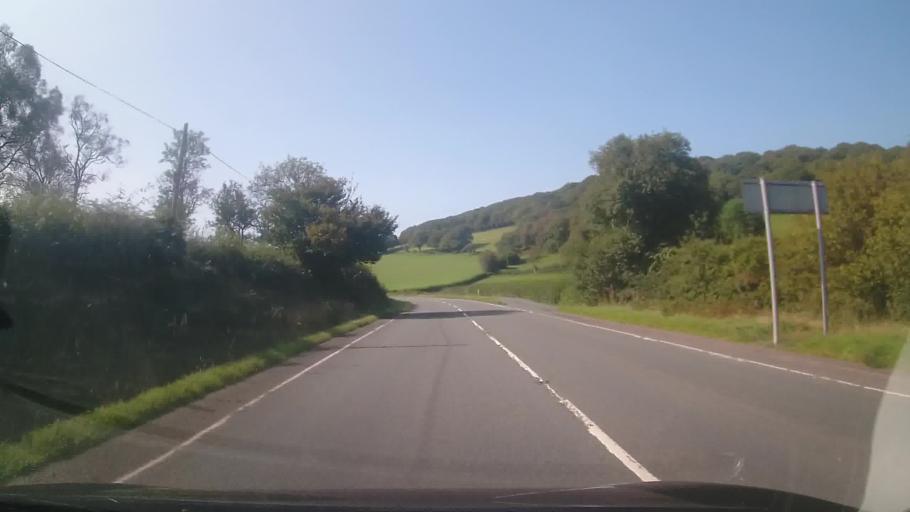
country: GB
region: Wales
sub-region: Sir Powys
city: Rhayader
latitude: 52.1461
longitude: -3.5874
